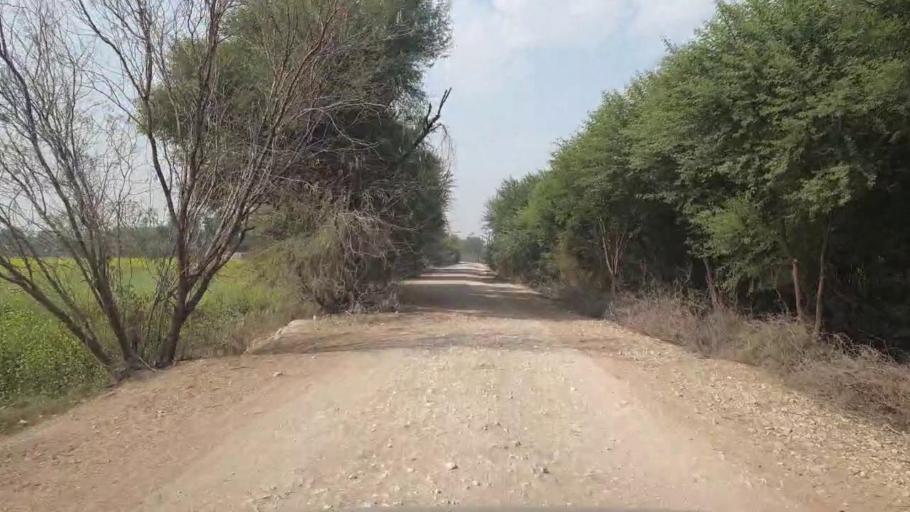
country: PK
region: Sindh
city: Hala
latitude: 25.7724
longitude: 68.4410
